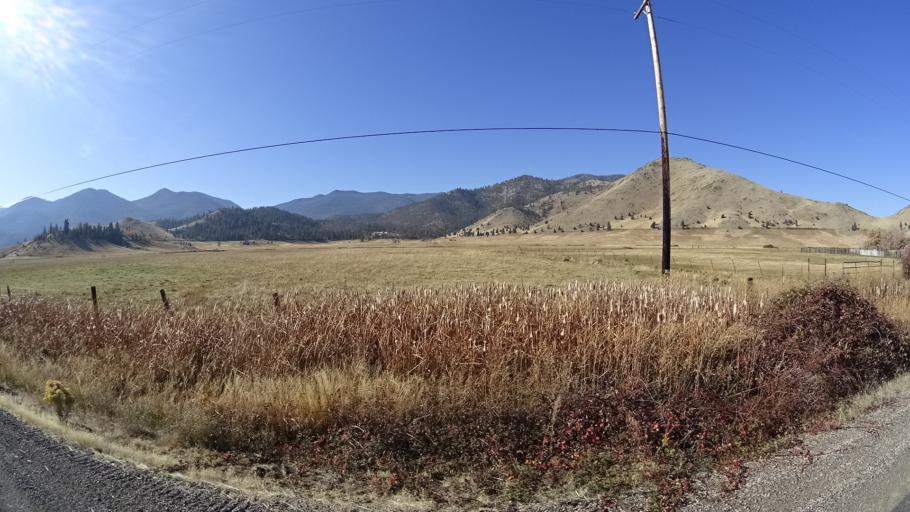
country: US
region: California
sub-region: Siskiyou County
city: Weed
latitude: 41.4571
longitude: -122.4605
